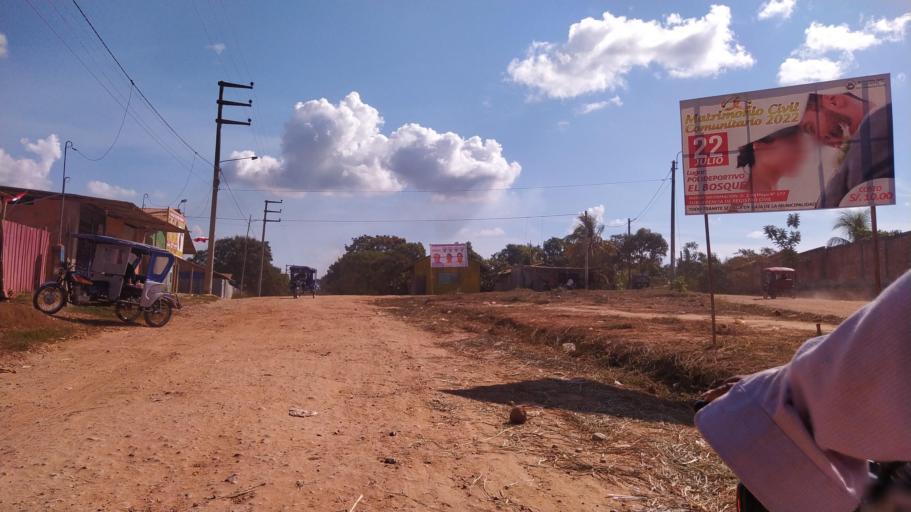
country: PE
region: Ucayali
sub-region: Provincia de Coronel Portillo
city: Puerto Callao
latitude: -8.3590
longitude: -74.5856
